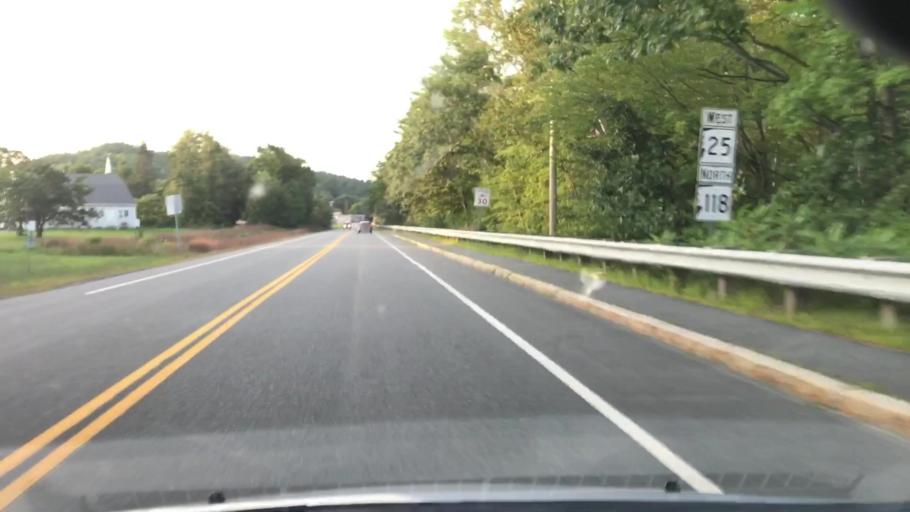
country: US
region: New Hampshire
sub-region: Grafton County
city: Rumney
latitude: 43.9219
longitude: -71.8900
